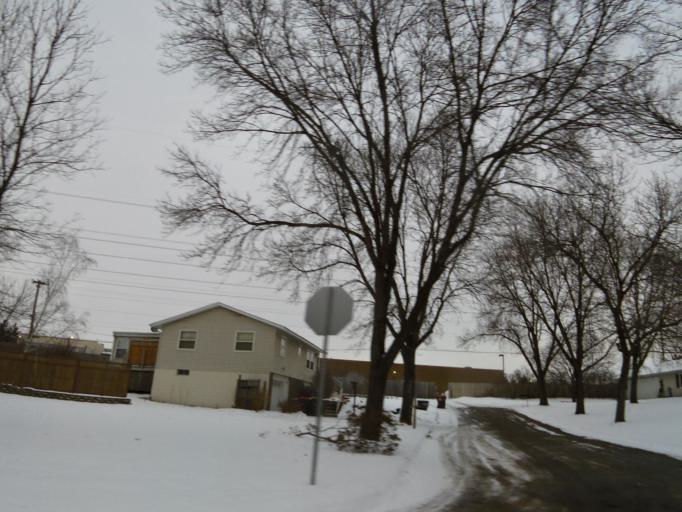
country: US
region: Minnesota
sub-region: Washington County
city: Oak Park Heights
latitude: 45.0320
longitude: -92.8090
